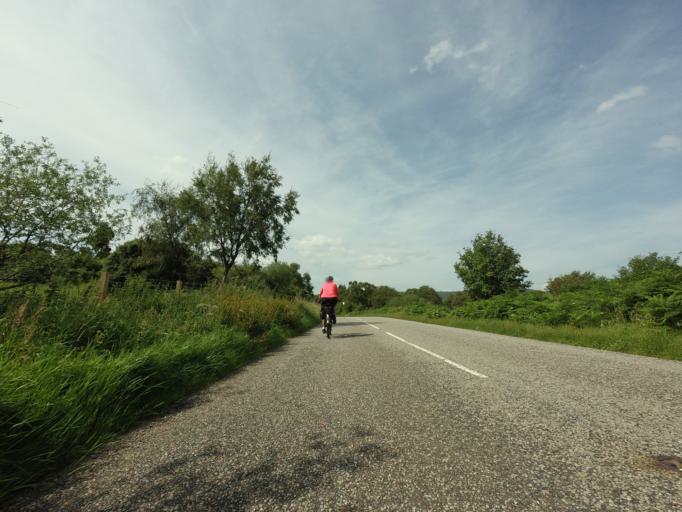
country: GB
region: Scotland
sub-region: Highland
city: Alness
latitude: 57.8576
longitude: -4.2314
